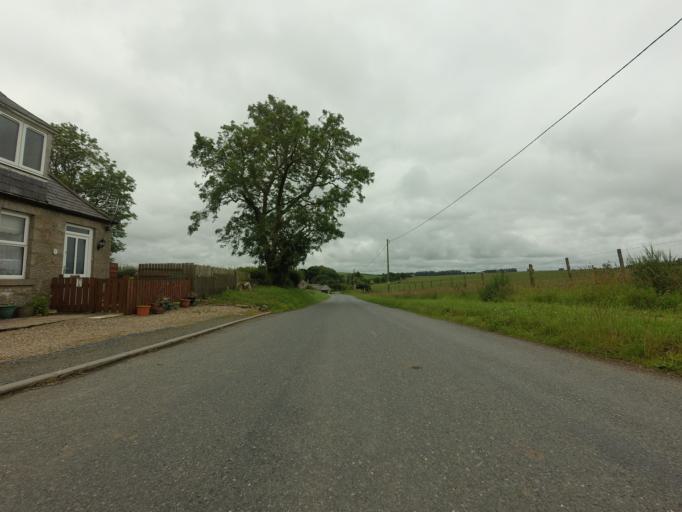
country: GB
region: Scotland
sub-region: Aberdeenshire
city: Rosehearty
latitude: 57.5392
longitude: -2.1887
